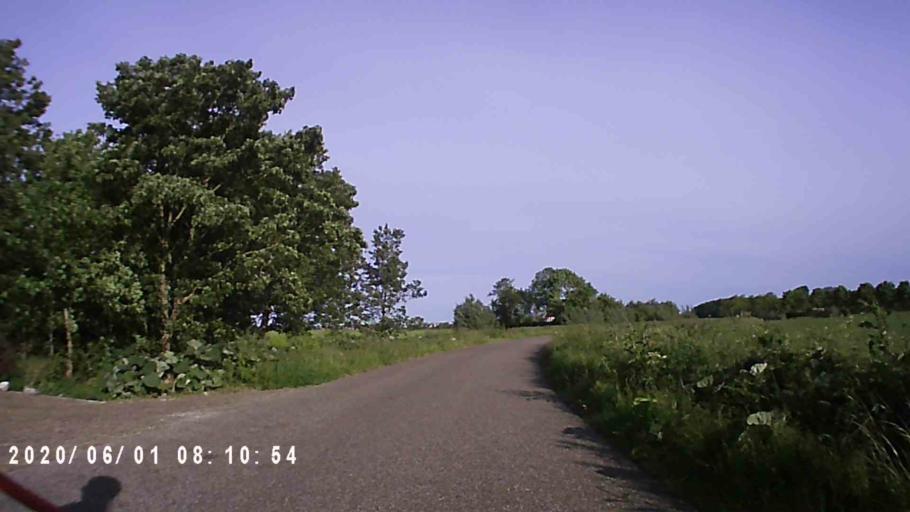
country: NL
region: Friesland
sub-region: Gemeente Ferwerderadiel
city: Burdaard
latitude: 53.2873
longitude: 5.8851
